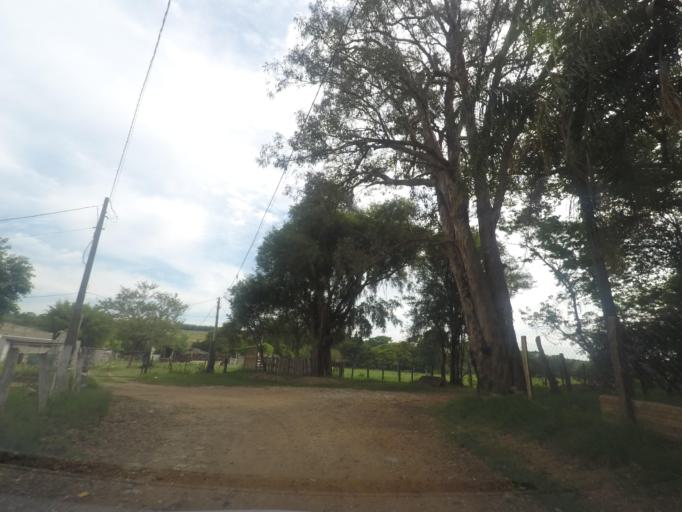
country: BR
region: Sao Paulo
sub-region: Sumare
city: Sumare
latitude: -22.7961
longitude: -47.2526
